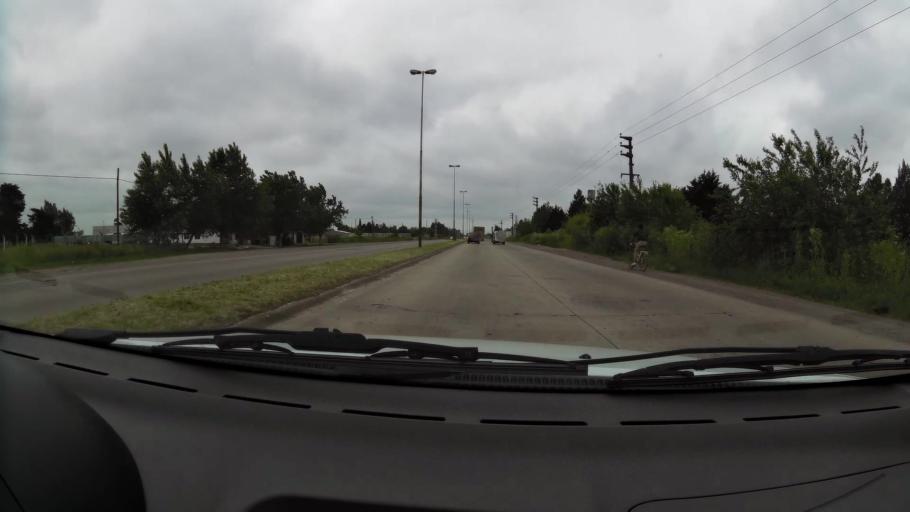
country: AR
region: Buenos Aires
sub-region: Partido de Brandsen
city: Brandsen
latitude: -35.0430
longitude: -58.1007
